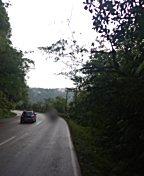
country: CR
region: San Jose
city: Dulce Nombre de Jesus
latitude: 10.0825
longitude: -83.9818
